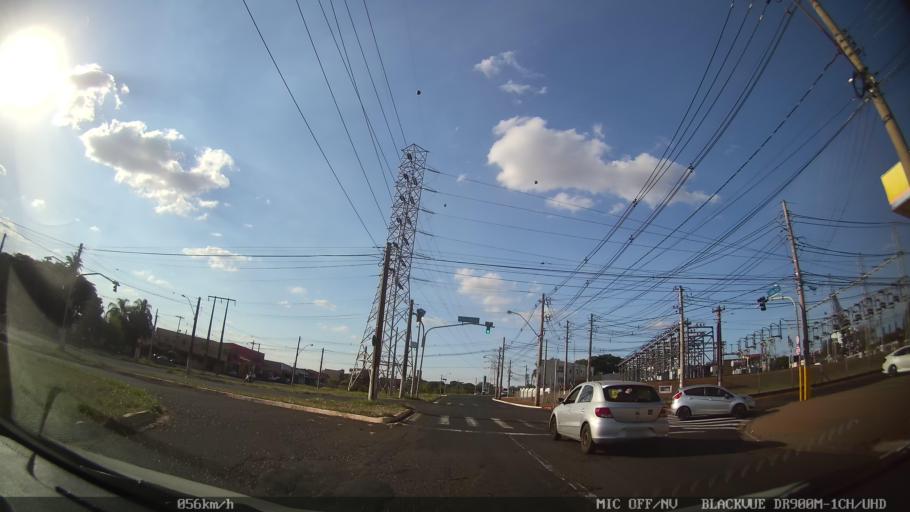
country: BR
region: Sao Paulo
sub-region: Ribeirao Preto
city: Ribeirao Preto
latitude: -21.1956
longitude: -47.7777
